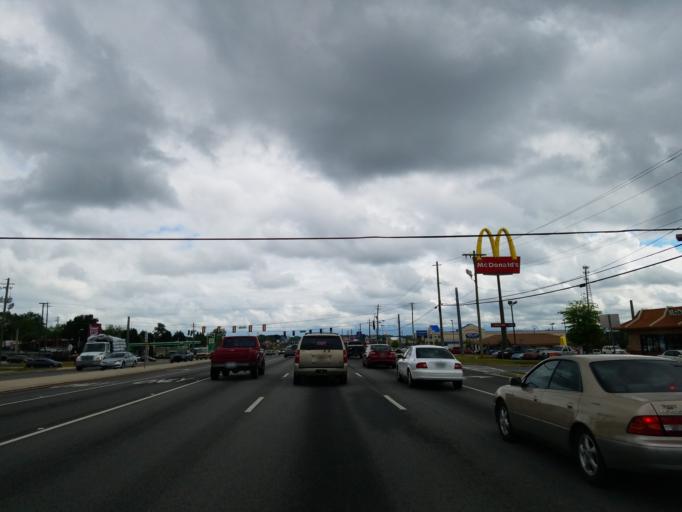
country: US
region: Georgia
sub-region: Spalding County
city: Experiment
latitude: 33.2757
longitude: -84.2914
